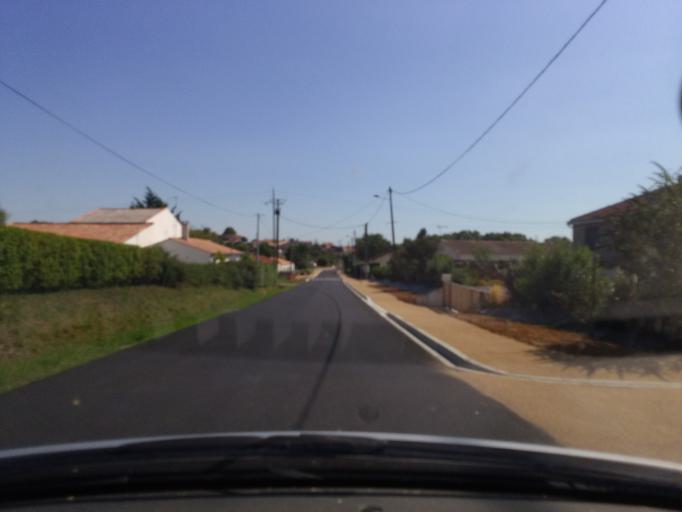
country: FR
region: Pays de la Loire
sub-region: Departement de la Vendee
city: Triaize
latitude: 46.4106
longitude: -1.2698
